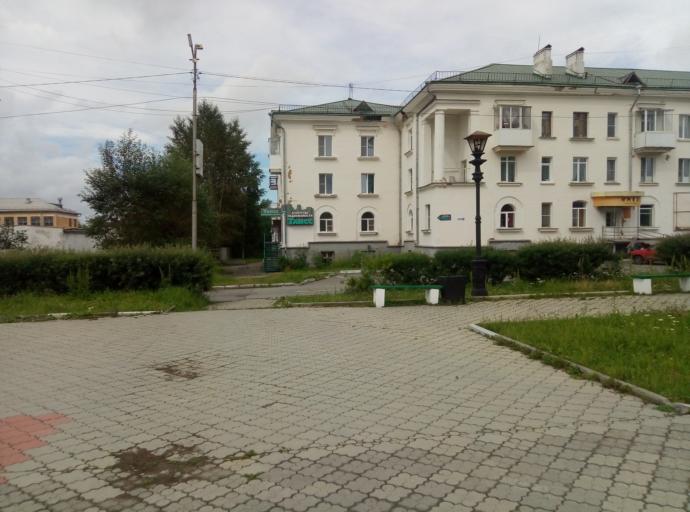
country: RU
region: Sverdlovsk
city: Krasnotur'insk
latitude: 59.7629
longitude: 60.1930
